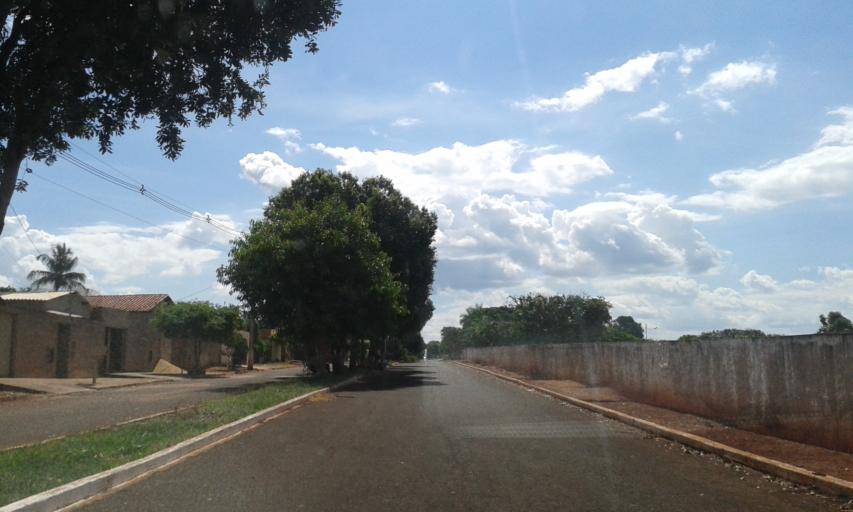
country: BR
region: Minas Gerais
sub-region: Santa Vitoria
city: Santa Vitoria
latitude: -18.8440
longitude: -50.1155
